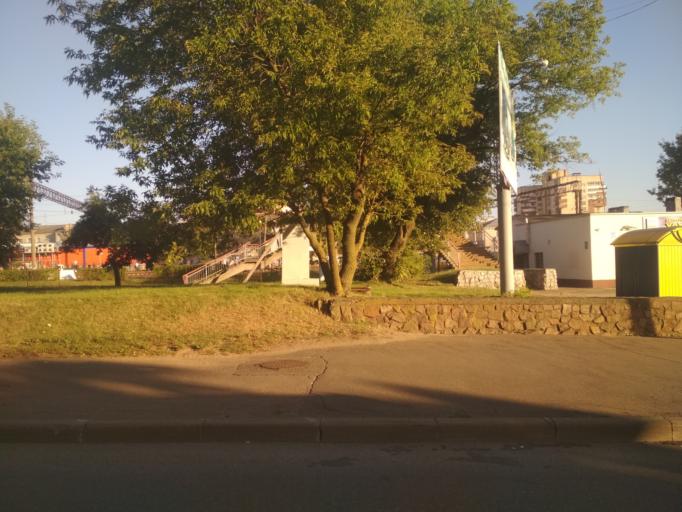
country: BY
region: Minsk
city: Minsk
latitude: 53.8918
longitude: 27.5856
